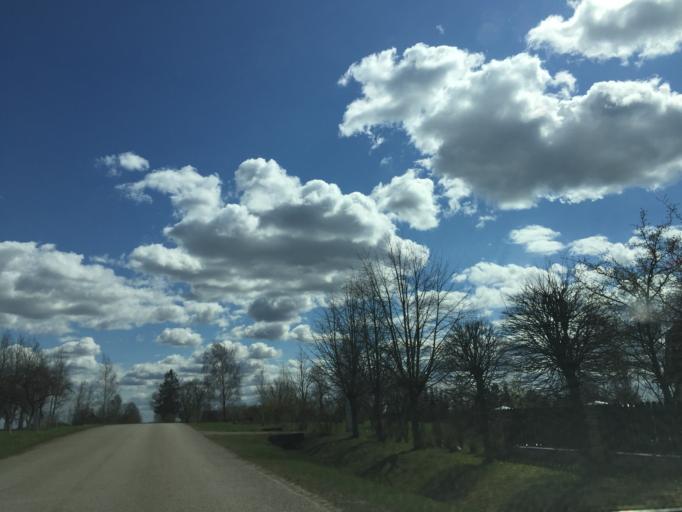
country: LV
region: Rezekne
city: Rezekne
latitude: 56.5622
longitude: 27.1431
